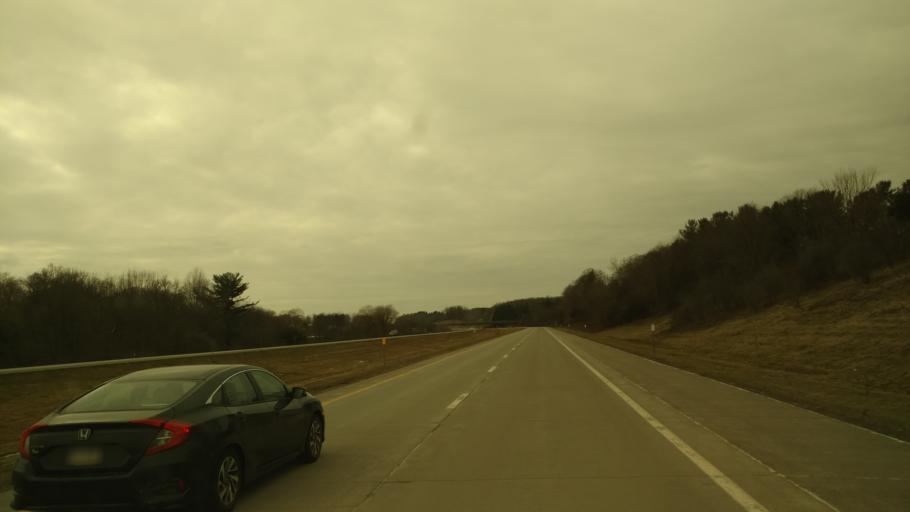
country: US
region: New York
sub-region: Chautauqua County
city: Lakewood
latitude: 42.1523
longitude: -79.4162
